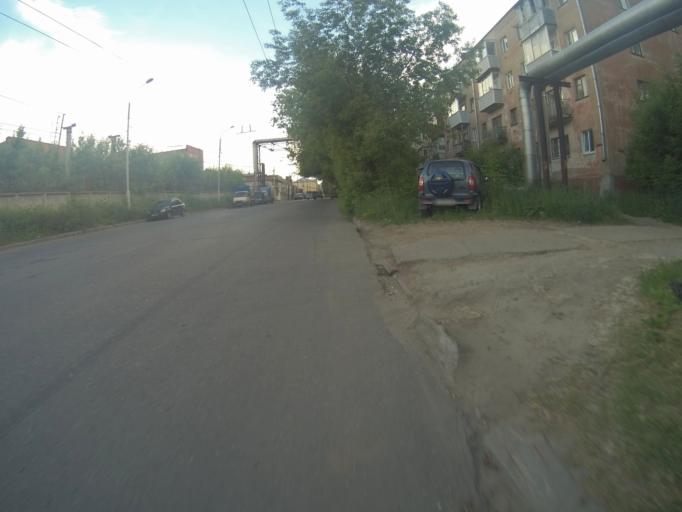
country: RU
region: Vladimir
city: Vladimir
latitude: 56.1524
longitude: 40.3798
